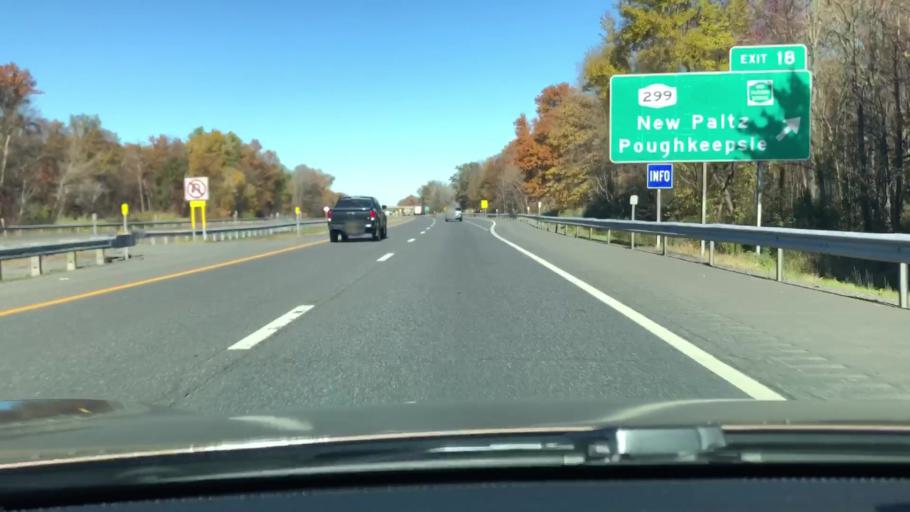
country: US
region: New York
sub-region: Ulster County
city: New Paltz
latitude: 41.7301
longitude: -74.0666
